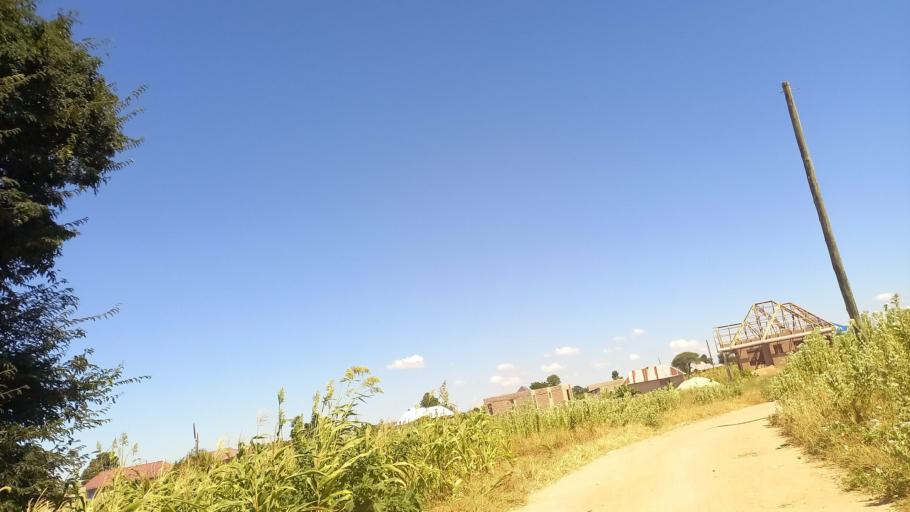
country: TZ
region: Dodoma
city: Dodoma
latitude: -6.1115
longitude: 35.7006
